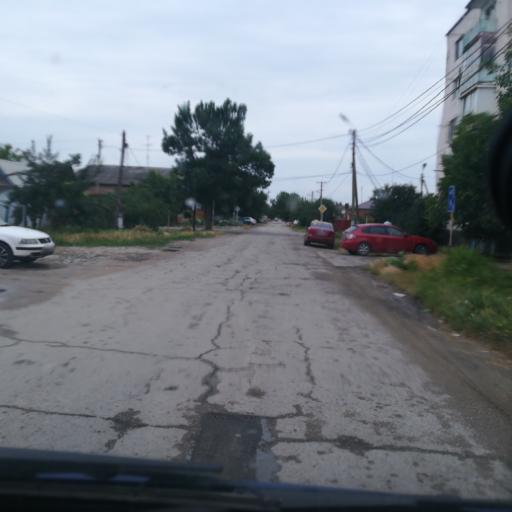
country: RU
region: Krasnodarskiy
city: Slavyansk-na-Kubani
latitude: 45.2623
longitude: 38.1268
